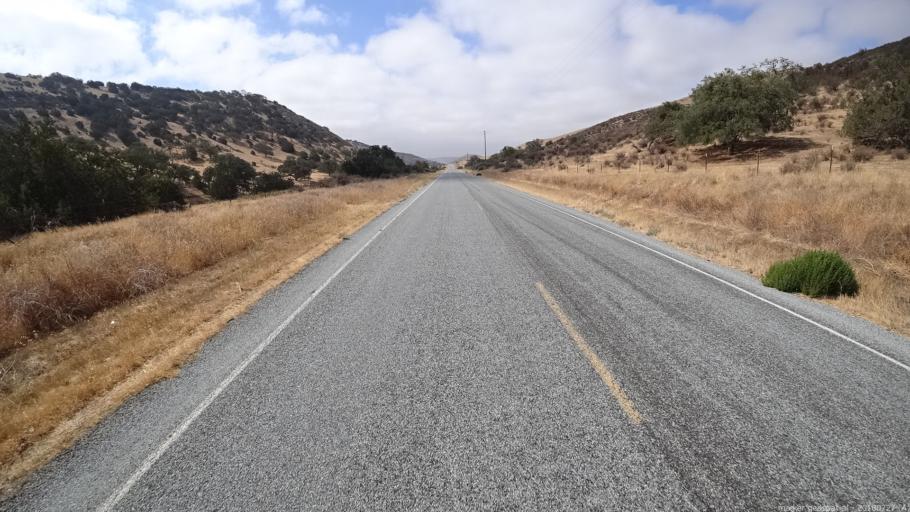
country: US
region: California
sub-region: Monterey County
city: King City
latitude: 36.2938
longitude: -121.0531
